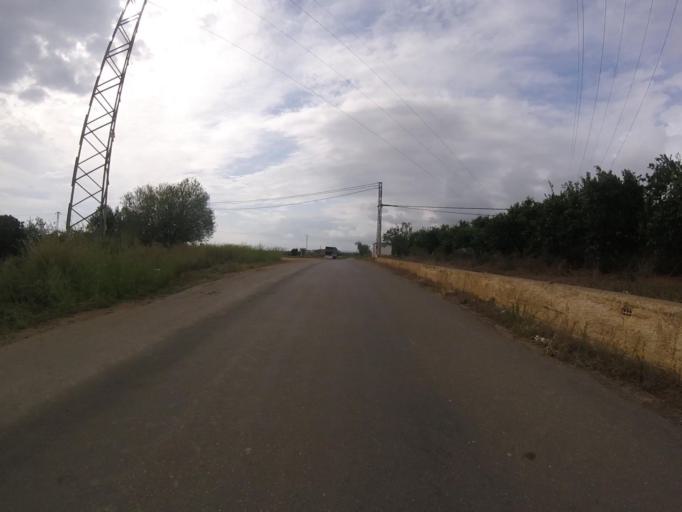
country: ES
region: Valencia
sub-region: Provincia de Castello
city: Torreblanca
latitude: 40.2076
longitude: 0.1840
